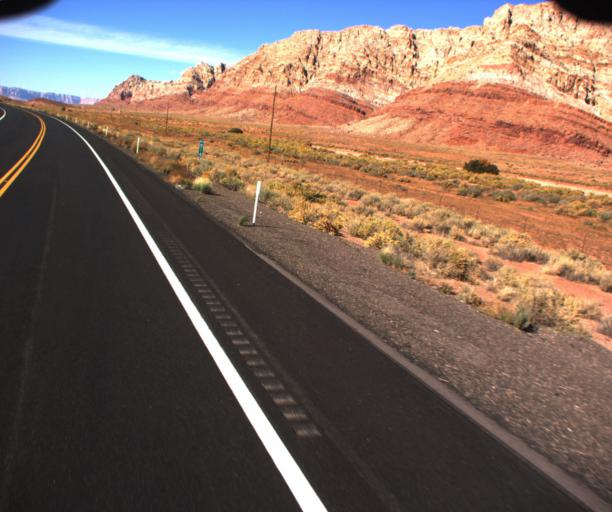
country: US
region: Arizona
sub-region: Coconino County
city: LeChee
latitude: 36.5085
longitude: -111.5851
